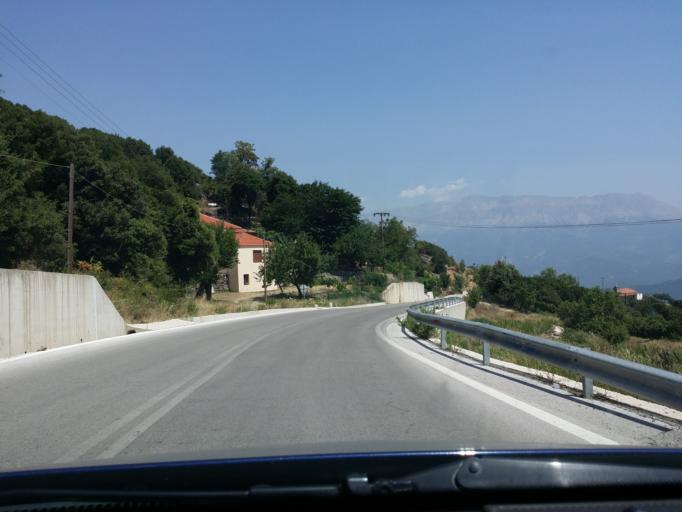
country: GR
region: Epirus
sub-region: Nomos Artas
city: Agios Dimitrios
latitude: 39.3321
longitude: 21.0001
